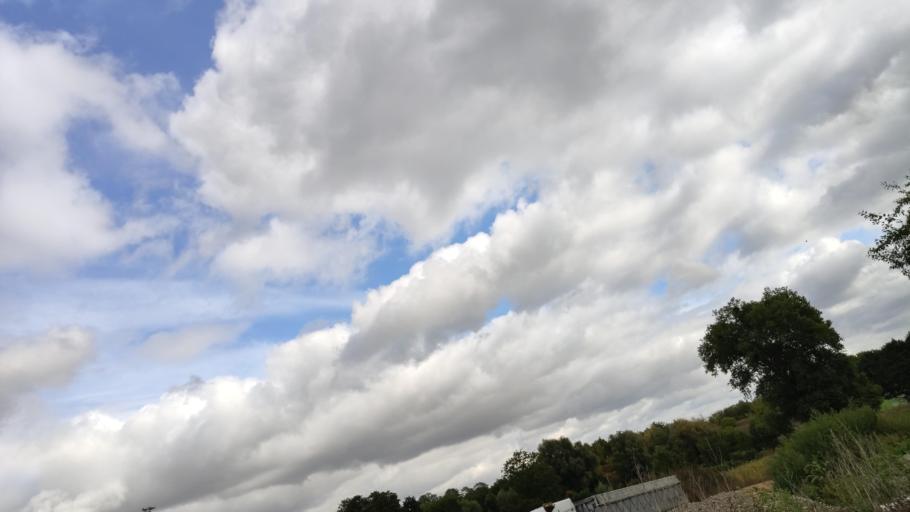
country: PL
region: Kujawsko-Pomorskie
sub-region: Powiat zninski
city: Barcin
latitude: 52.8442
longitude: 17.9539
